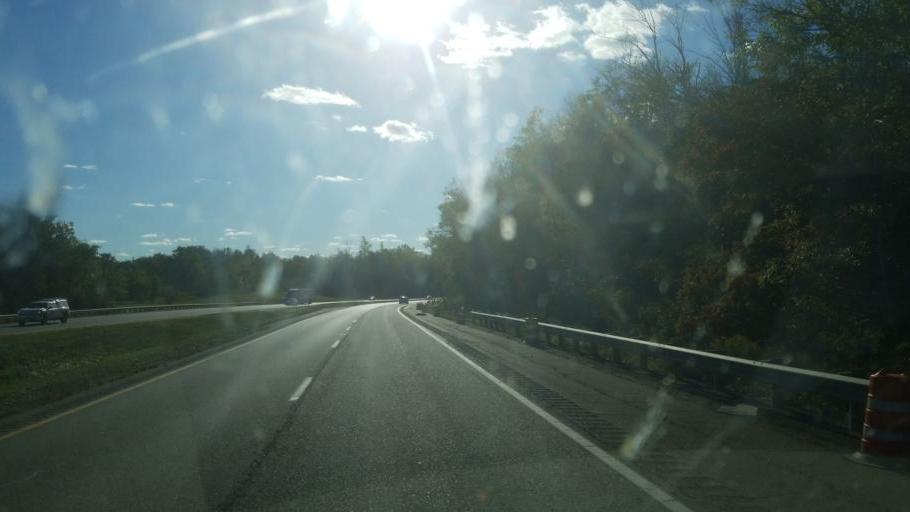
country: US
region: Ohio
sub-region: Belmont County
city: Bethesda
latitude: 40.0582
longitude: -81.1079
